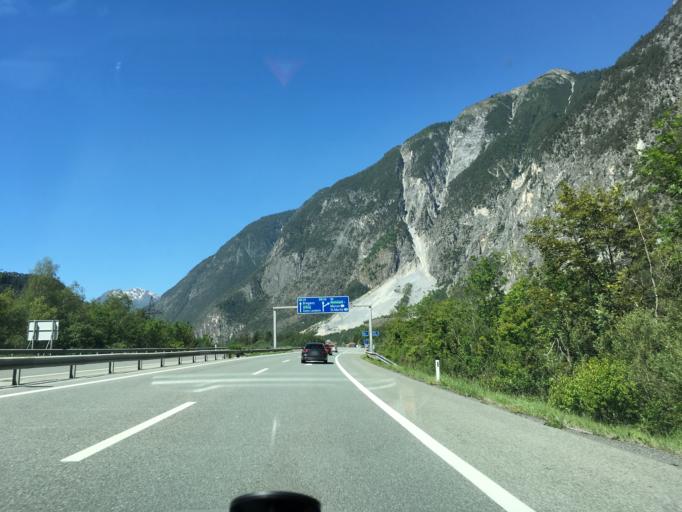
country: AT
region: Tyrol
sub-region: Politischer Bezirk Landeck
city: Zams
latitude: 47.1740
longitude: 10.6101
